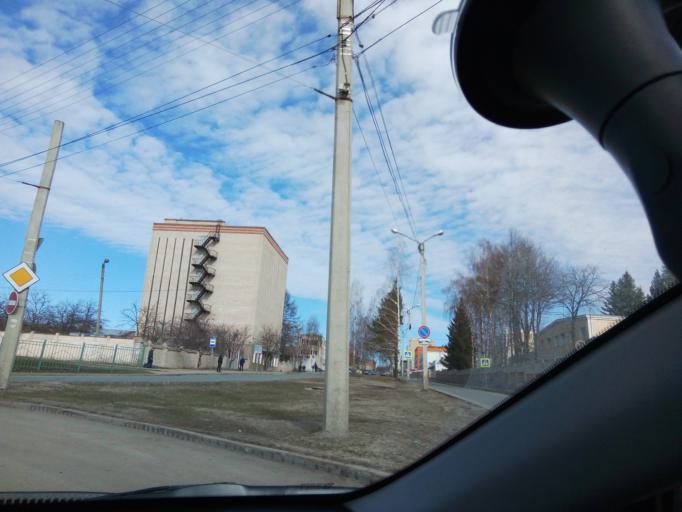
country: RU
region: Chuvashia
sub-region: Cheboksarskiy Rayon
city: Cheboksary
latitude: 56.1117
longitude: 47.2477
